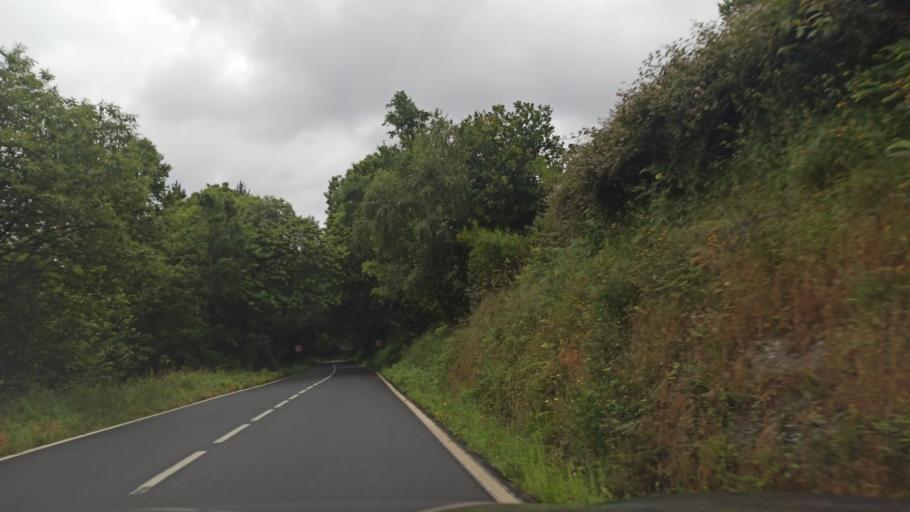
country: ES
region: Galicia
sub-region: Provincia da Coruna
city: Santiso
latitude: 42.7822
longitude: -8.0810
